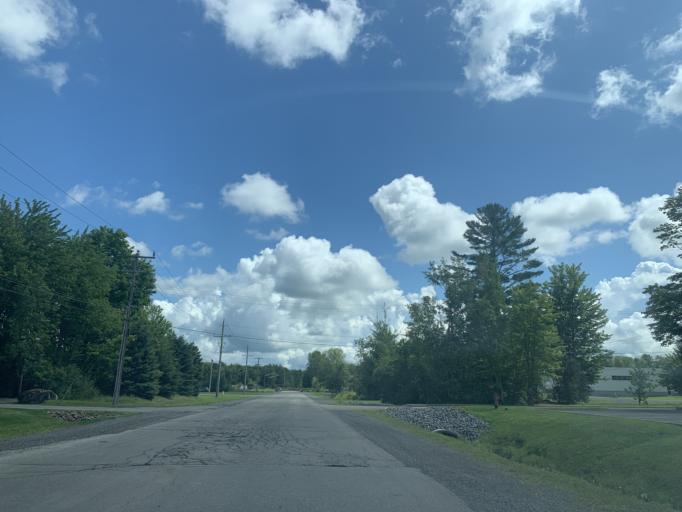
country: CA
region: Ontario
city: Hawkesbury
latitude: 45.6000
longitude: -74.5889
